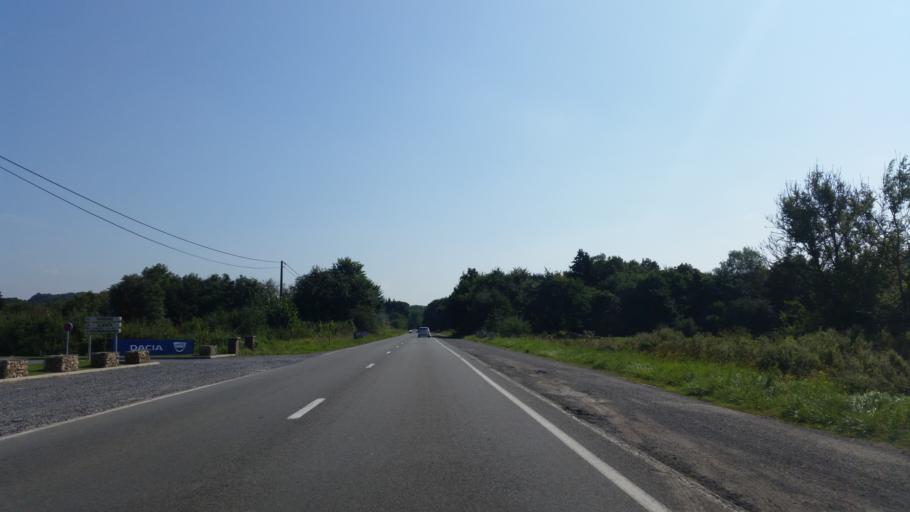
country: BE
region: Wallonia
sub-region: Province du Luxembourg
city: Durbuy
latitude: 50.3391
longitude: 5.4455
